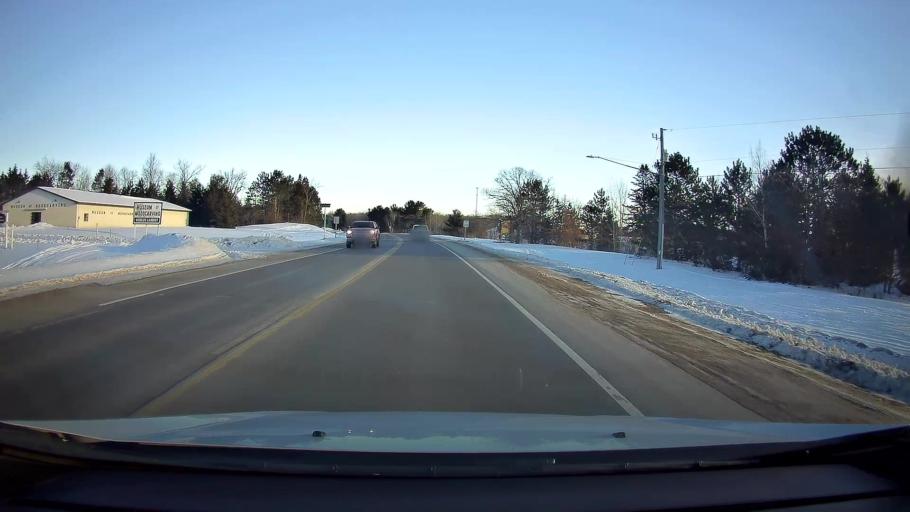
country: US
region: Wisconsin
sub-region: Washburn County
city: Shell Lake
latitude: 45.7480
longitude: -91.9185
